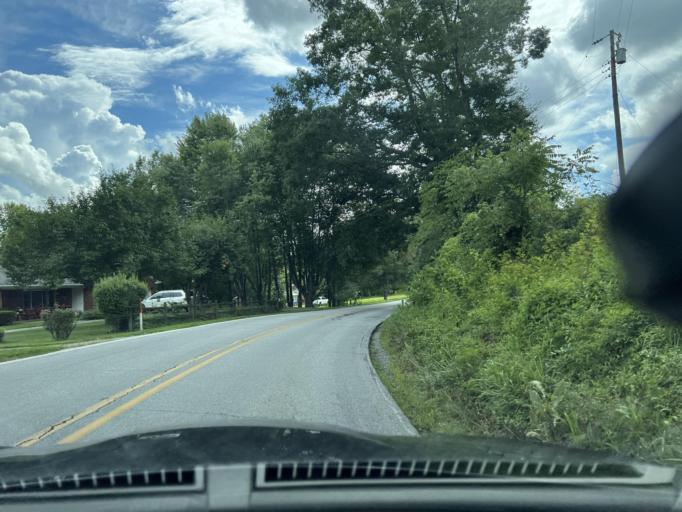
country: US
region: North Carolina
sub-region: Henderson County
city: Hoopers Creek
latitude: 35.4401
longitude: -82.4608
